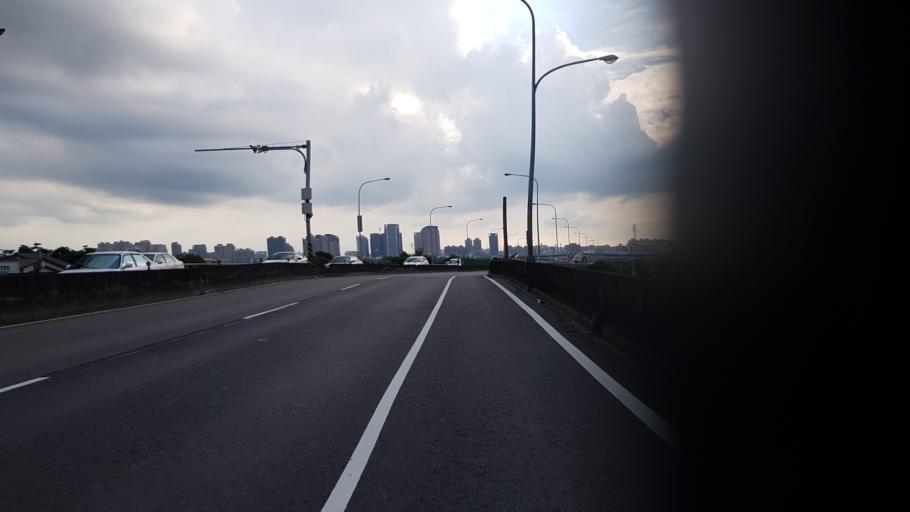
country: TW
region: Taiwan
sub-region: Hsinchu
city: Zhubei
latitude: 24.8110
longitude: 121.0218
